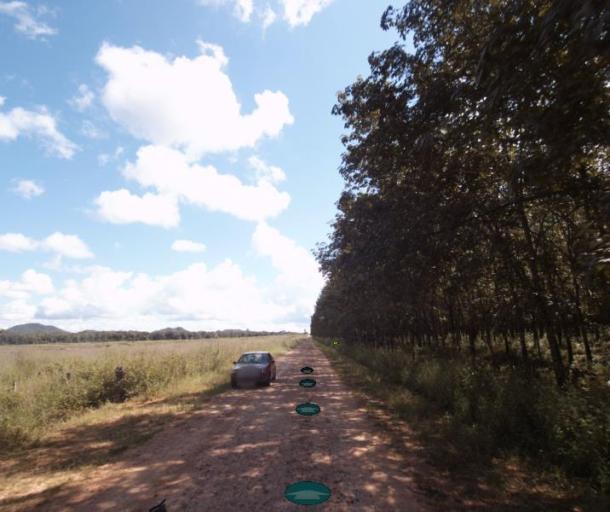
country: BR
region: Goias
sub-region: Pirenopolis
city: Pirenopolis
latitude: -15.7782
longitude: -49.0384
